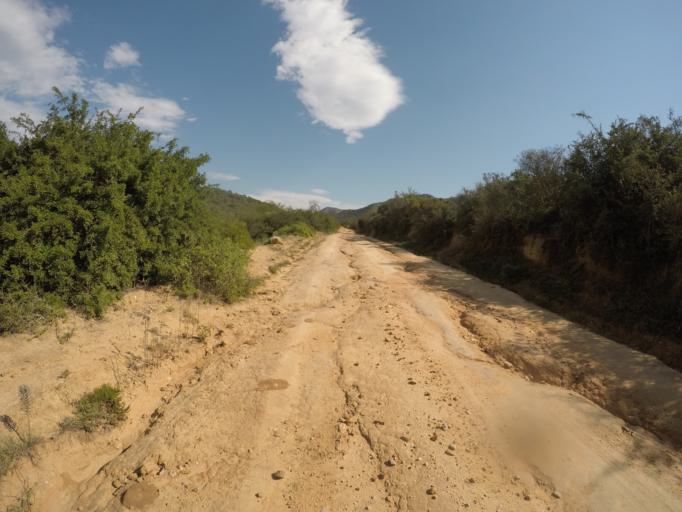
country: ZA
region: Eastern Cape
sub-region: Cacadu District Municipality
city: Kareedouw
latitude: -33.6546
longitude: 24.4153
